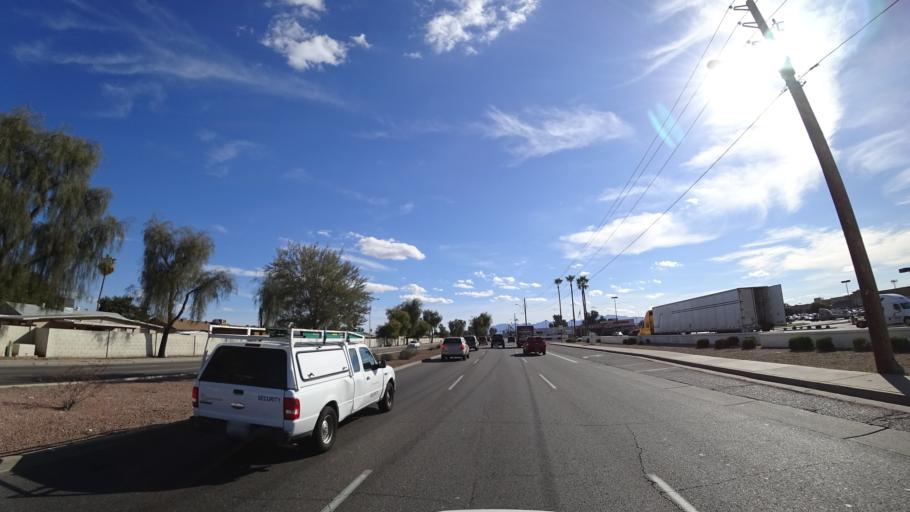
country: US
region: Arizona
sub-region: Maricopa County
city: Tolleson
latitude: 33.4719
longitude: -112.2207
